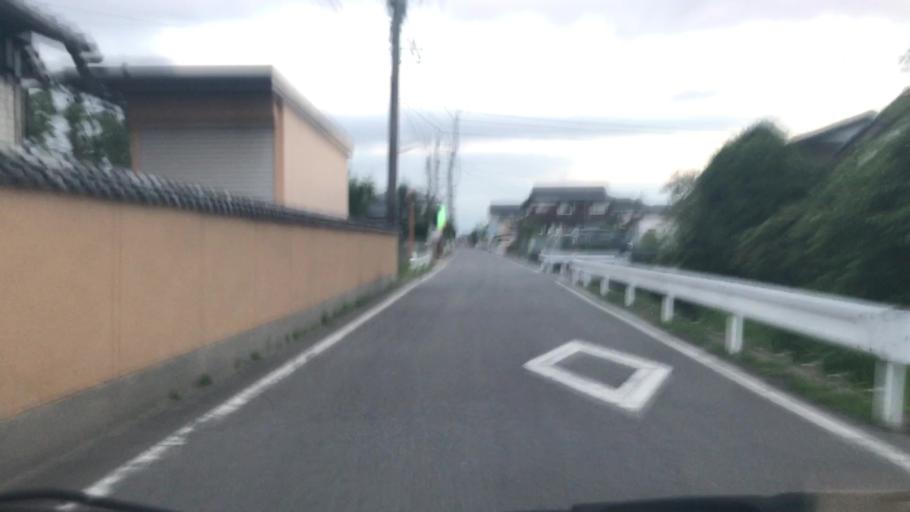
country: JP
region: Saga Prefecture
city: Saga-shi
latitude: 33.2332
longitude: 130.3017
